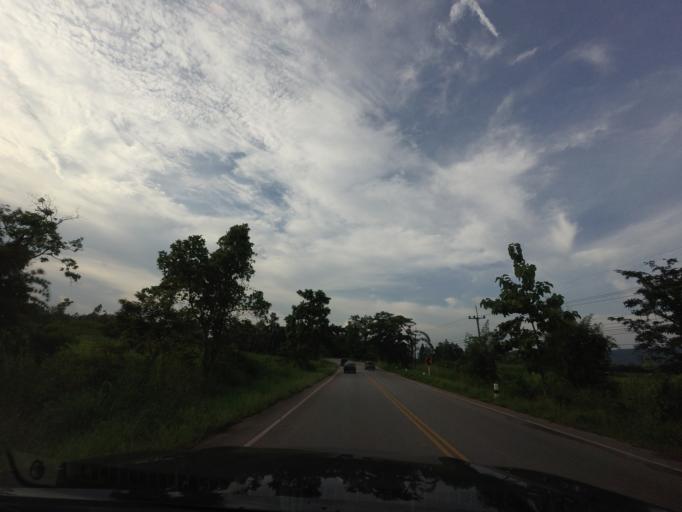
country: TH
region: Changwat Udon Thani
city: Nam Som
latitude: 17.8346
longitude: 102.2608
